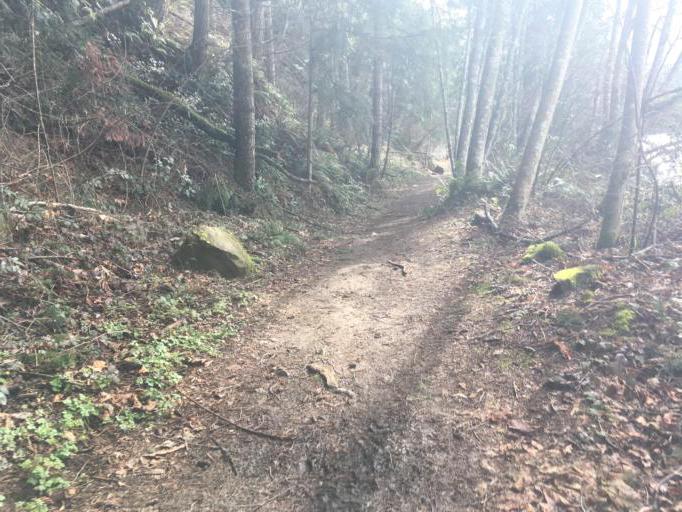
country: US
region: Washington
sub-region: Whatcom County
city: Sudden Valley
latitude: 48.6921
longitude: -122.2931
